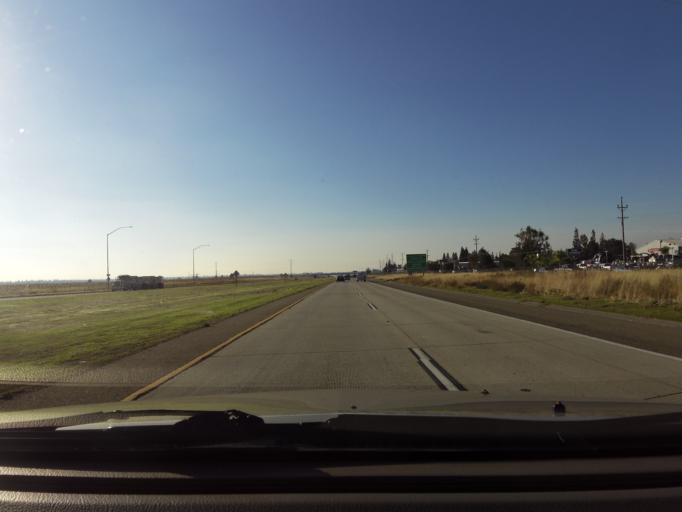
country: US
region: California
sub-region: Madera County
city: Bonadelle Ranchos-Madera Ranchos
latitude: 36.9030
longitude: -119.7928
